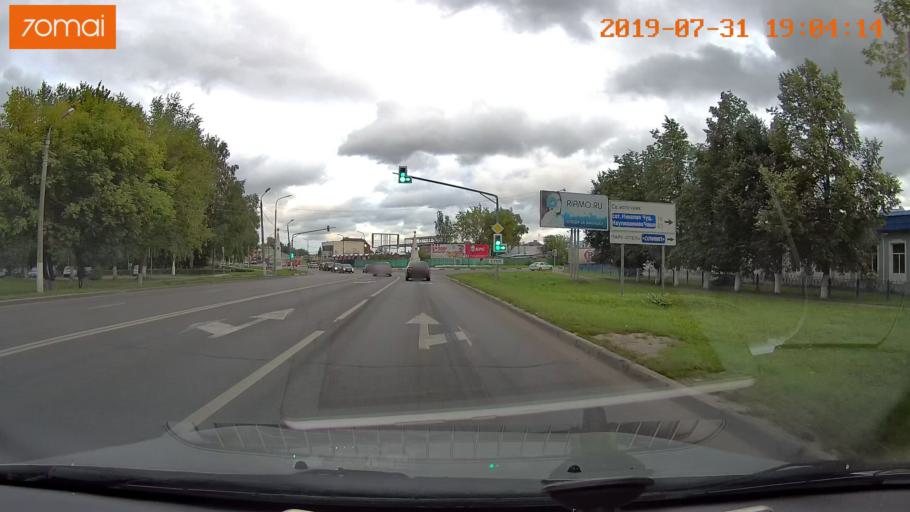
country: RU
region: Moskovskaya
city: Raduzhnyy
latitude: 55.1099
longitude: 38.7399
